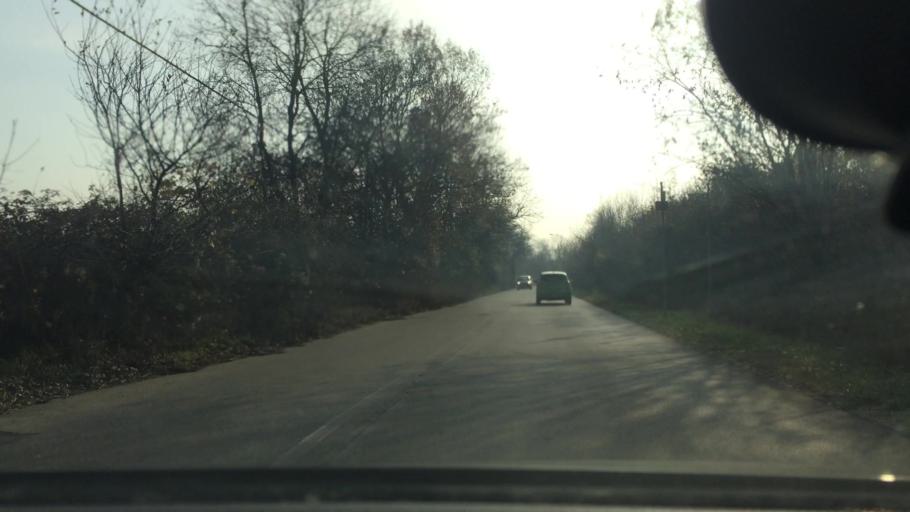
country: IT
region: Lombardy
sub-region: Provincia di Monza e Brianza
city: Villaggio del Sole
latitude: 45.6006
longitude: 9.0970
